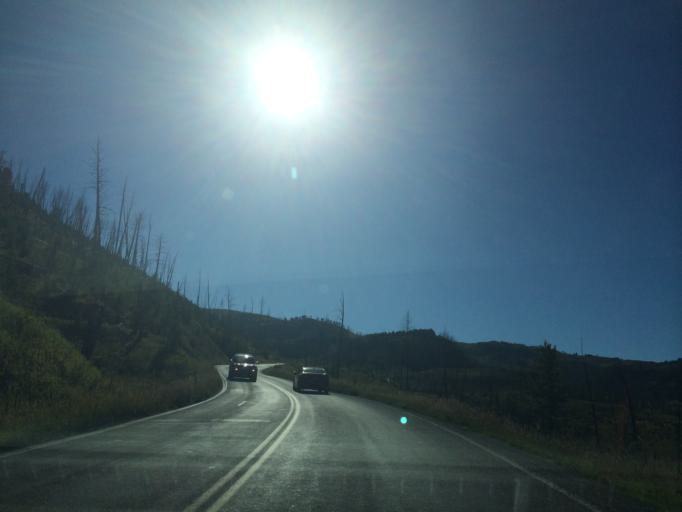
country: US
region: Montana
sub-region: Gallatin County
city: West Yellowstone
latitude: 44.9227
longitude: -110.4330
